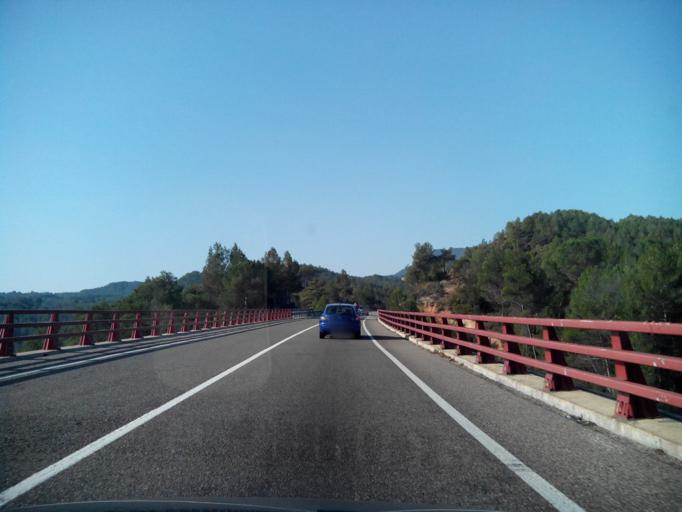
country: ES
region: Catalonia
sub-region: Provincia de Barcelona
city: Castellfollit del Boix
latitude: 41.6618
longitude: 1.7355
